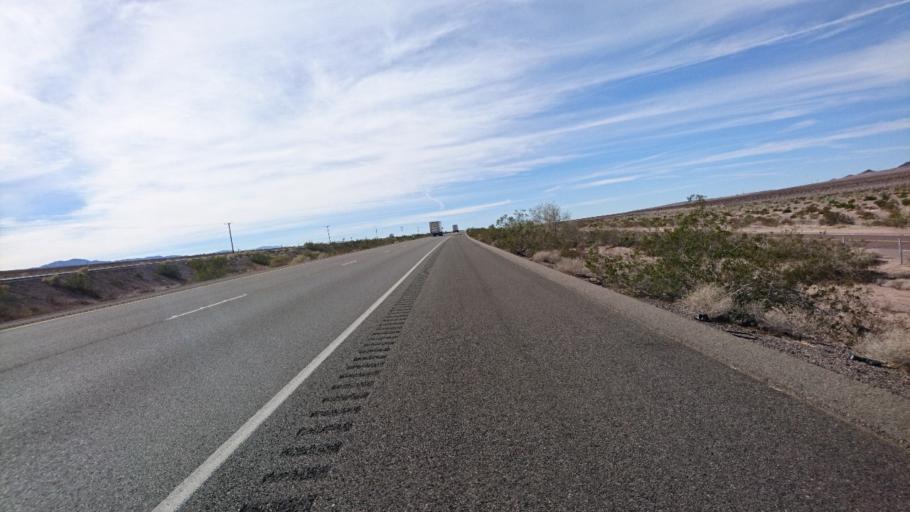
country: US
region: California
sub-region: San Bernardino County
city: Joshua Tree
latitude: 34.7265
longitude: -116.2402
